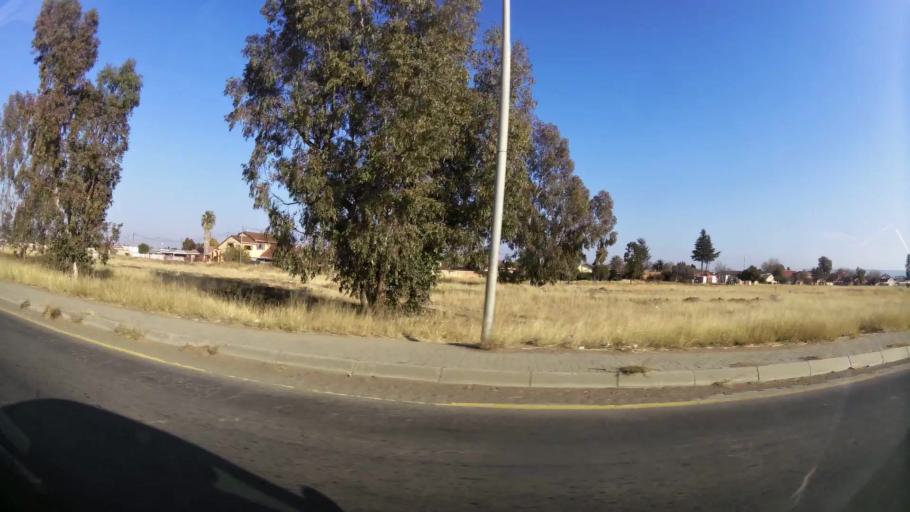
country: ZA
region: Orange Free State
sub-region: Mangaung Metropolitan Municipality
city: Bloemfontein
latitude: -29.1456
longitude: 26.2659
